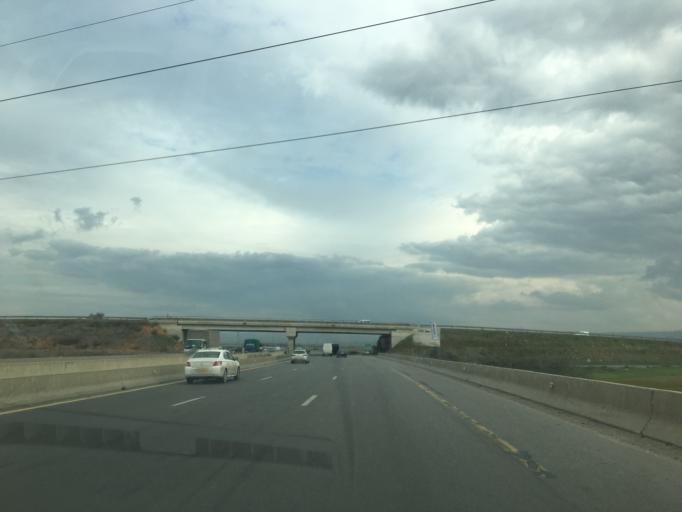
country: DZ
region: Bouira
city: Bouira
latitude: 36.3324
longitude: 3.9324
